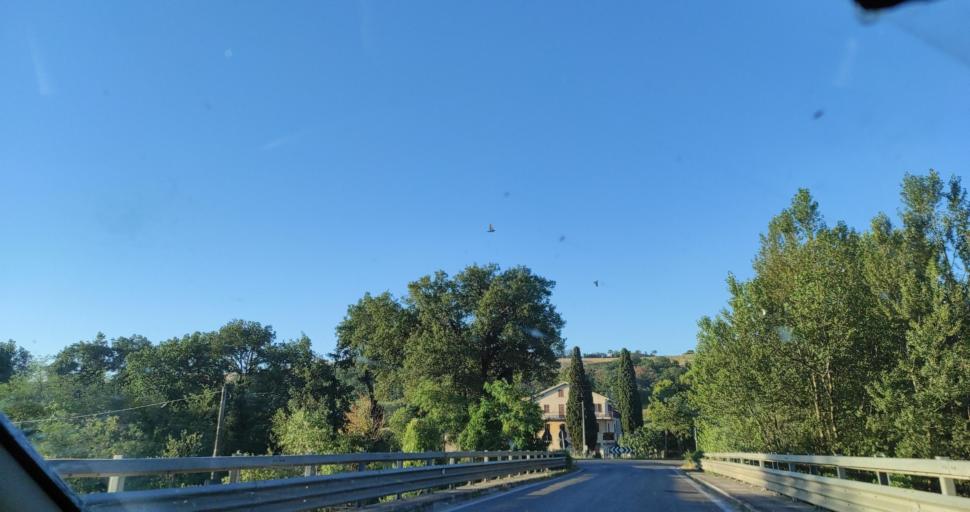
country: IT
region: The Marches
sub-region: Provincia di Macerata
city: Casette Verdini
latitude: 43.2324
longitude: 13.3710
